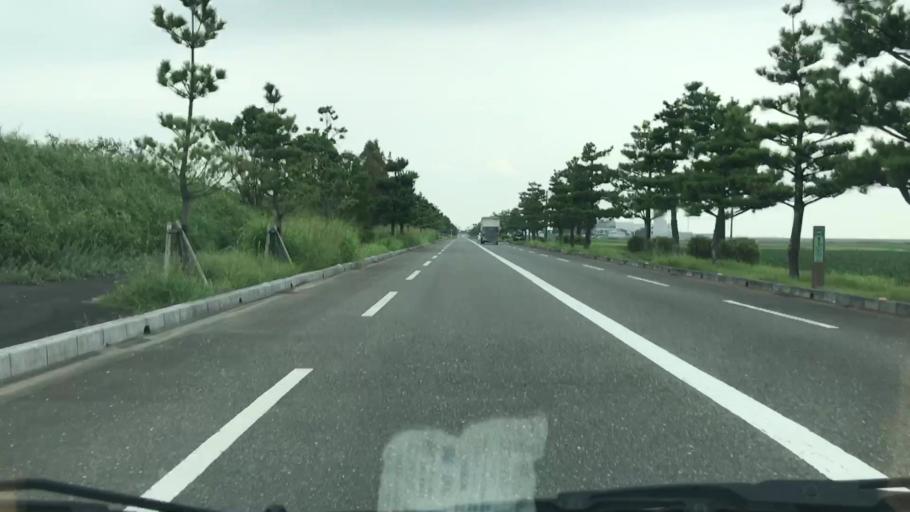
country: JP
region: Saga Prefecture
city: Okawa
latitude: 33.1579
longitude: 130.2953
